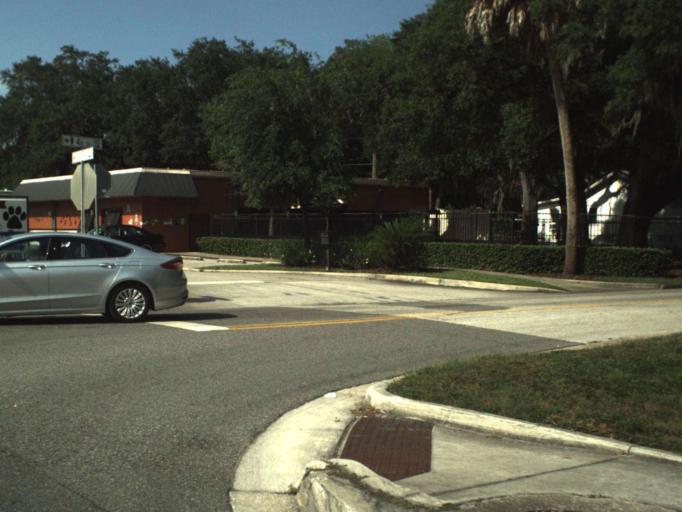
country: US
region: Florida
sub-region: Seminole County
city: Sanford
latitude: 28.8089
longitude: -81.2731
